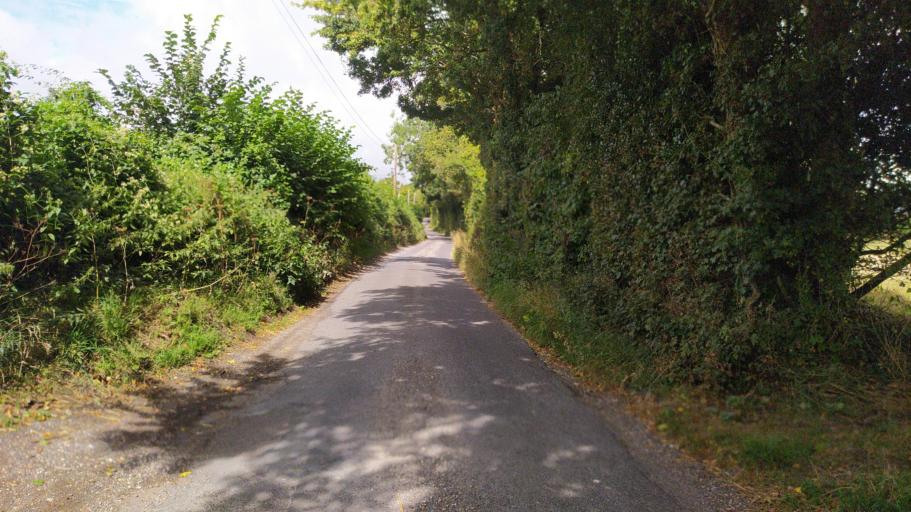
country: GB
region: England
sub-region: Hampshire
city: Petersfield
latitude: 50.9896
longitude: -0.9931
